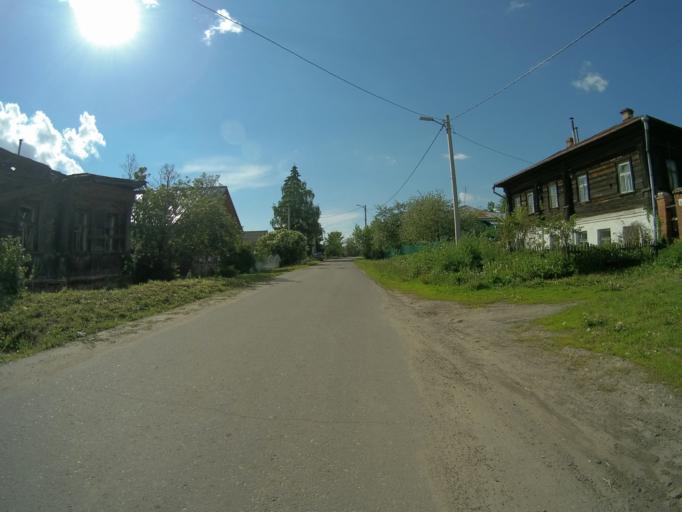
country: RU
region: Vladimir
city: Suzdal'
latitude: 56.4227
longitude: 40.4421
